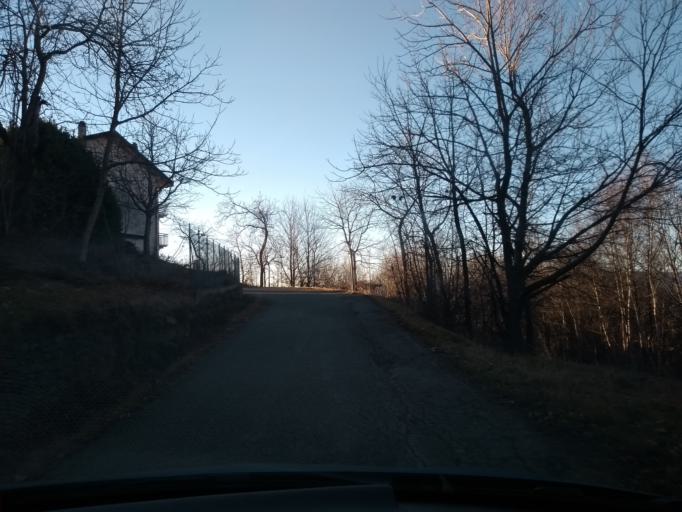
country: IT
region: Piedmont
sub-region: Provincia di Torino
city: Corio
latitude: 45.3213
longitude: 7.5457
